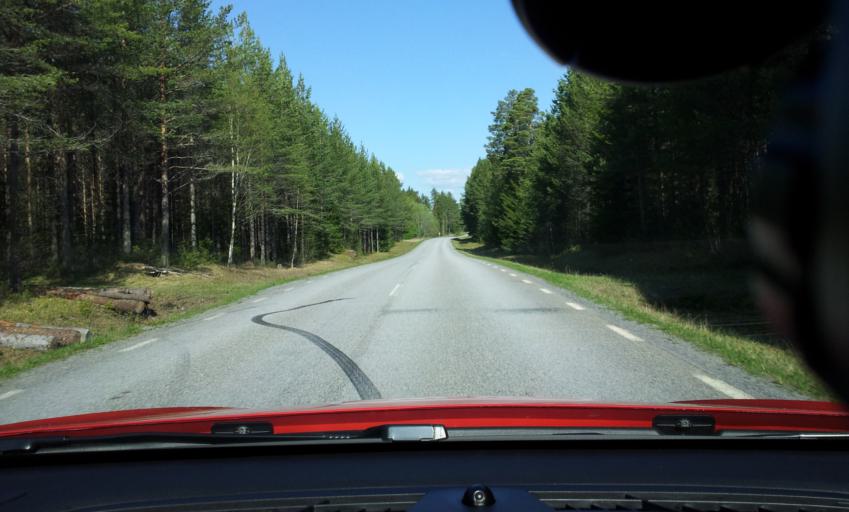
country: SE
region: Jaemtland
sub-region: Krokoms Kommun
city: Krokom
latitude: 63.1340
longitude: 14.2019
